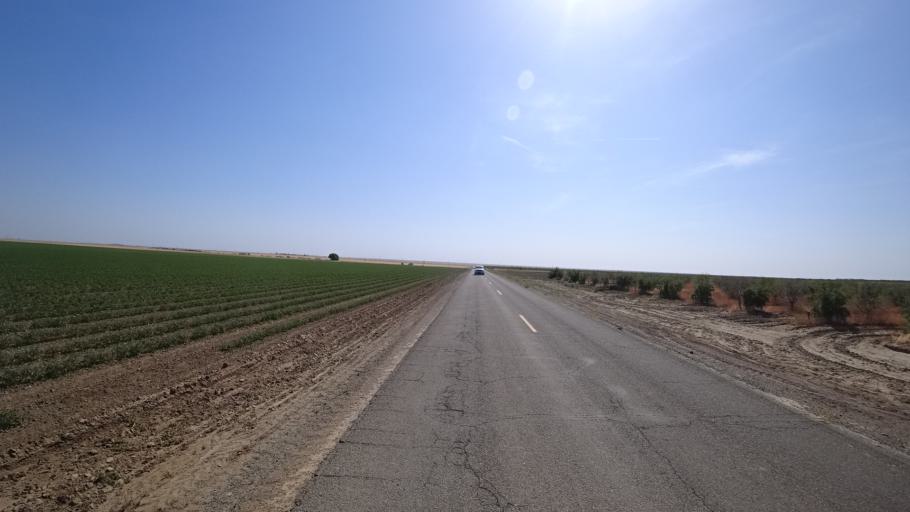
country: US
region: California
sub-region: Kings County
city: Kettleman City
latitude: 36.0363
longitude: -119.9732
